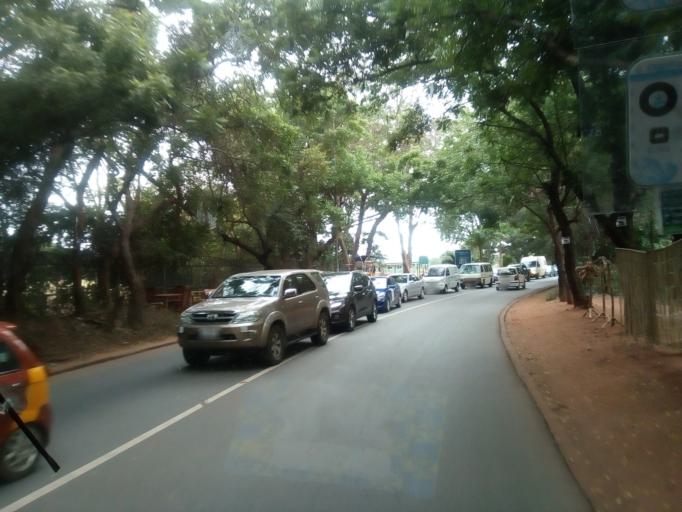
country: GH
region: Greater Accra
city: Dome
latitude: 5.6268
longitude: -0.2176
